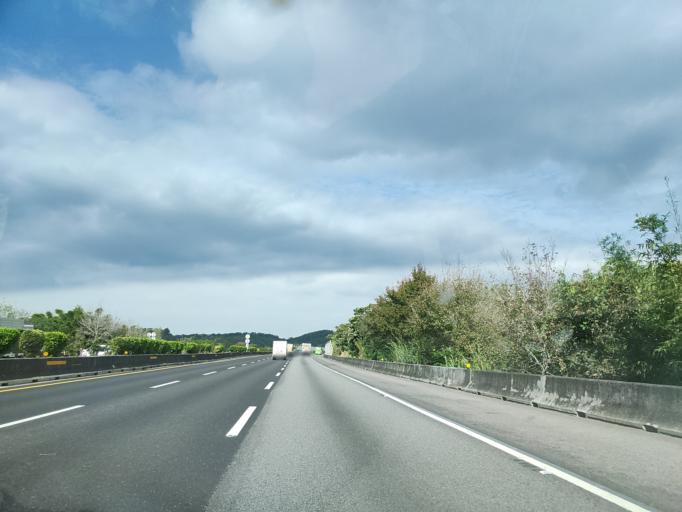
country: TW
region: Taiwan
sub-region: Miaoli
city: Miaoli
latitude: 24.6311
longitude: 120.8667
